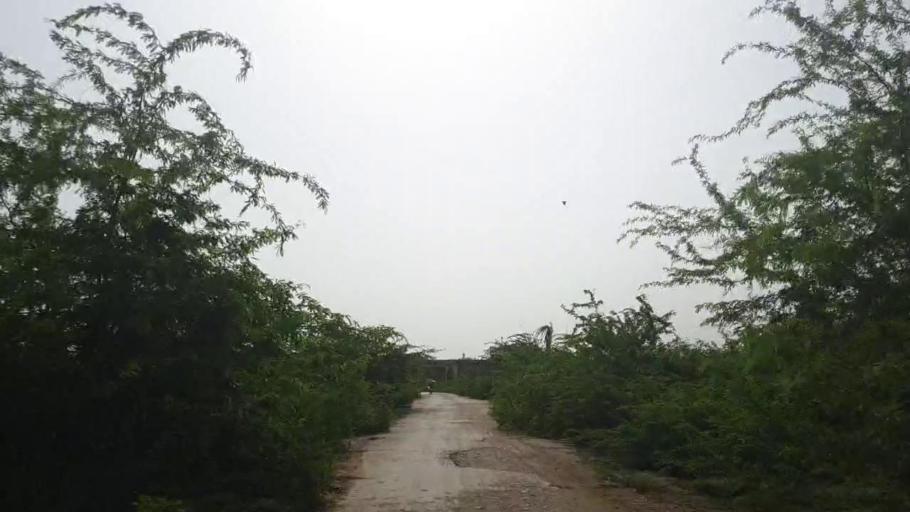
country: PK
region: Sindh
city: Nawabshah
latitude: 26.1110
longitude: 68.4414
